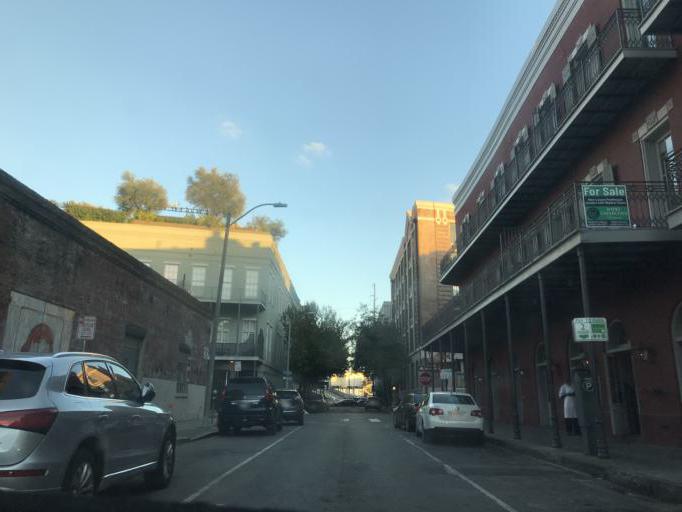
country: US
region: Louisiana
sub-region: Orleans Parish
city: New Orleans
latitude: 29.9462
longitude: -90.0663
